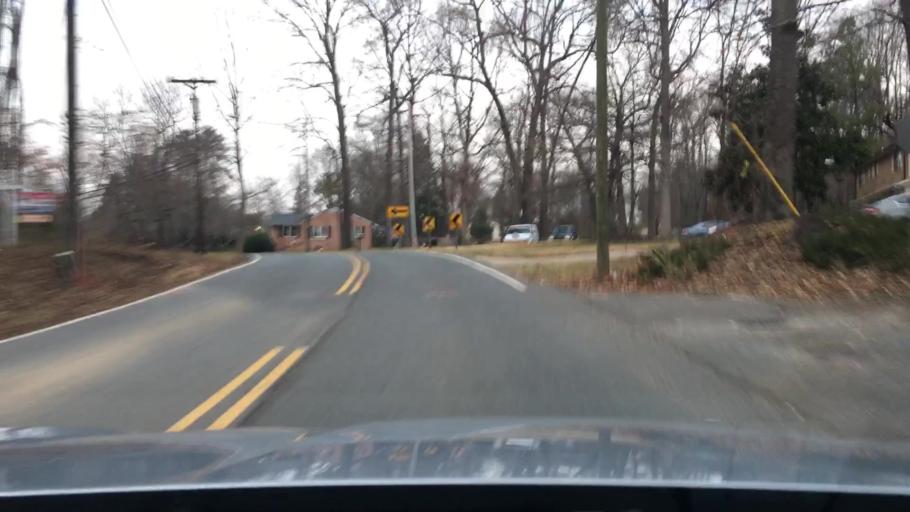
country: US
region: Maryland
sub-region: Prince George's County
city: Glenn Dale
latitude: 38.9960
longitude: -76.7756
